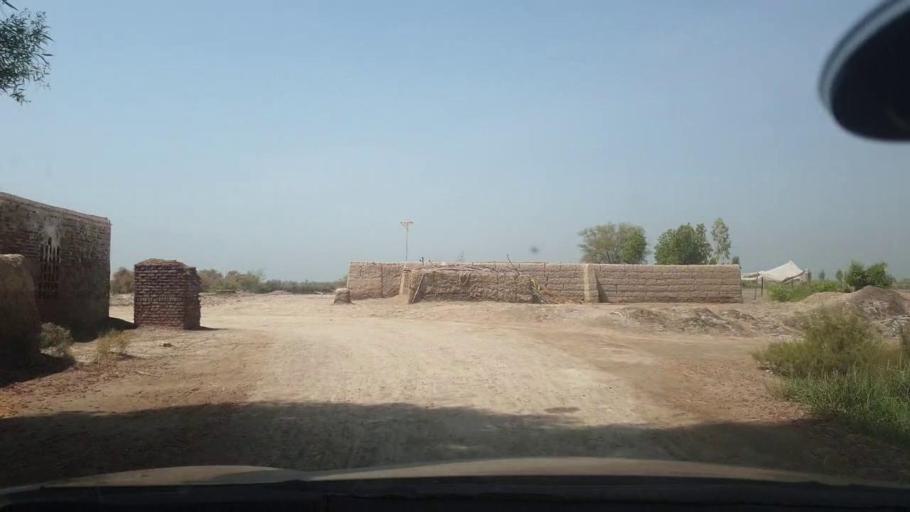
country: PK
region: Sindh
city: Shahdadkot
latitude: 27.7569
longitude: 67.9378
